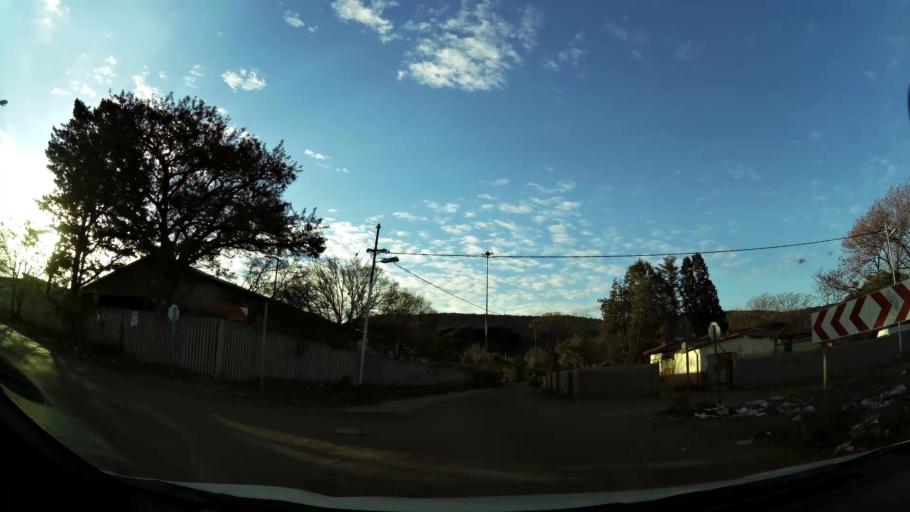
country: ZA
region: Gauteng
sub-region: City of Tshwane Metropolitan Municipality
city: Cullinan
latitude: -25.7085
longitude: 28.3659
